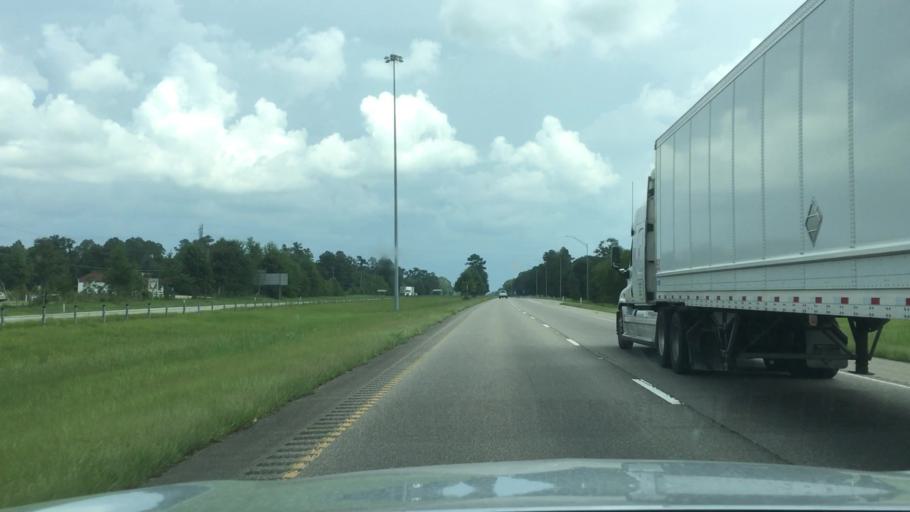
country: US
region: Mississippi
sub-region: Pearl River County
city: Picayune
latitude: 30.5450
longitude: -89.6486
